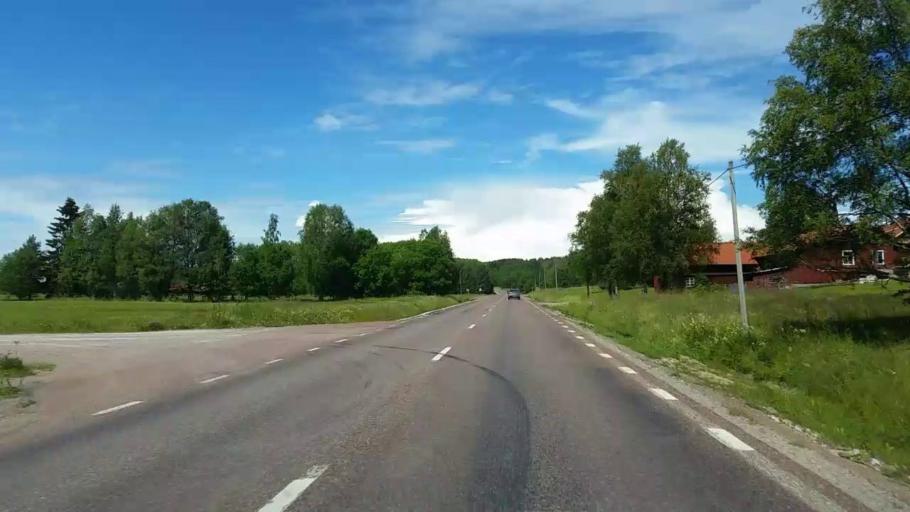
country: SE
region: Dalarna
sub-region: Rattviks Kommun
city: Raettvik
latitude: 61.0083
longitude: 15.2187
